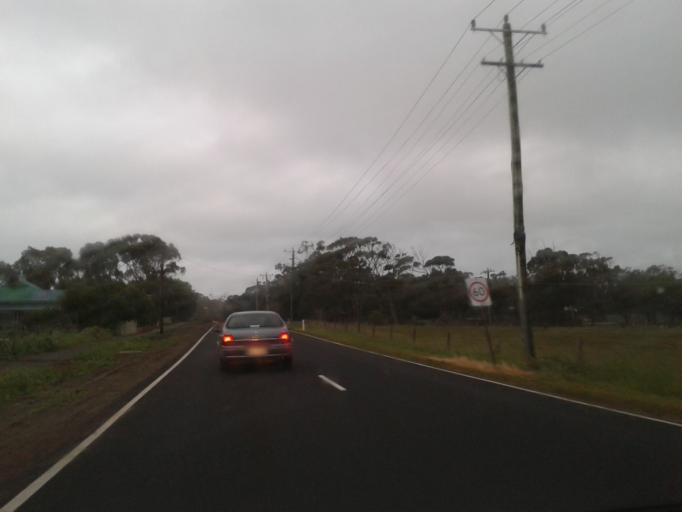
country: AU
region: Victoria
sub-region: Glenelg
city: Portland
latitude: -38.3405
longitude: 141.5809
